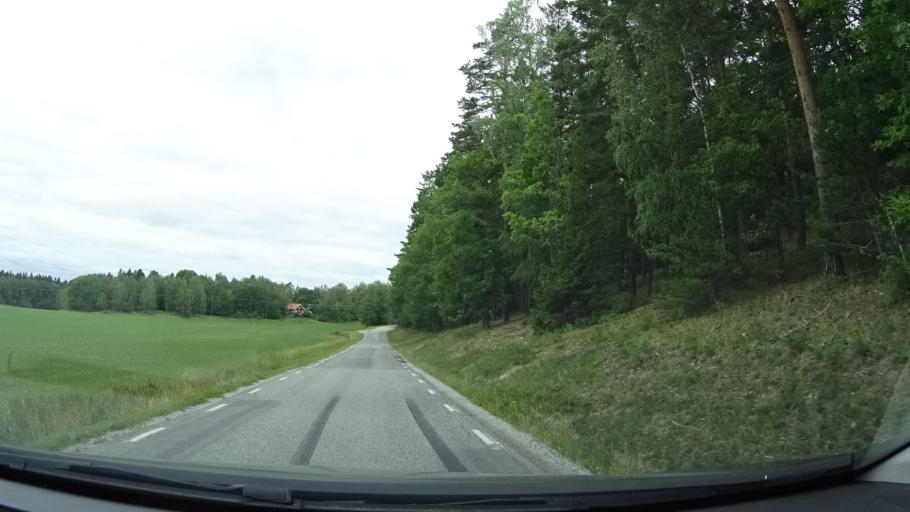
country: SE
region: Stockholm
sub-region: Varmdo Kommun
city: Mortnas
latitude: 59.3657
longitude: 18.4692
